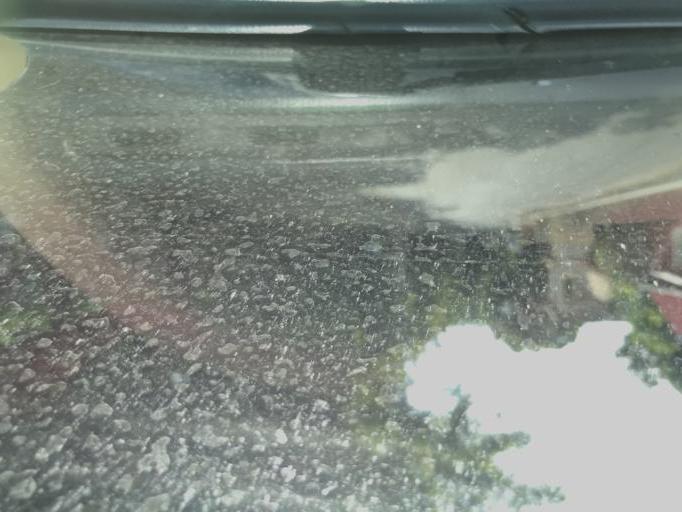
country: DO
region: Santiago
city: Santiago de los Caballeros
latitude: 19.4535
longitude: -70.7263
